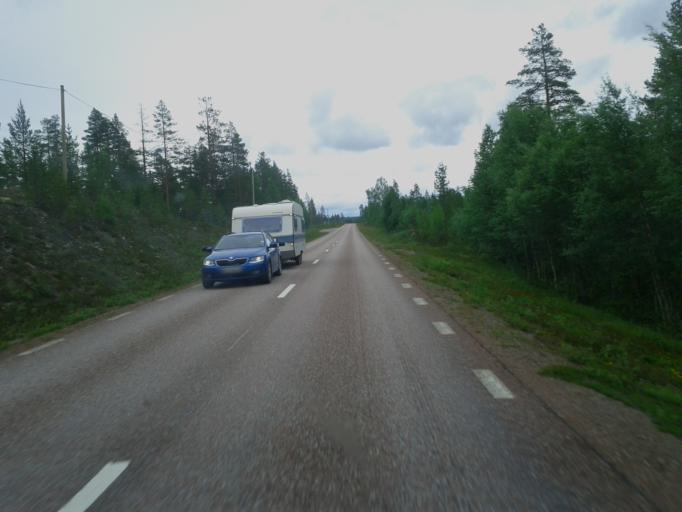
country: NO
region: Hedmark
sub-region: Trysil
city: Innbygda
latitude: 61.6965
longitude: 13.0440
